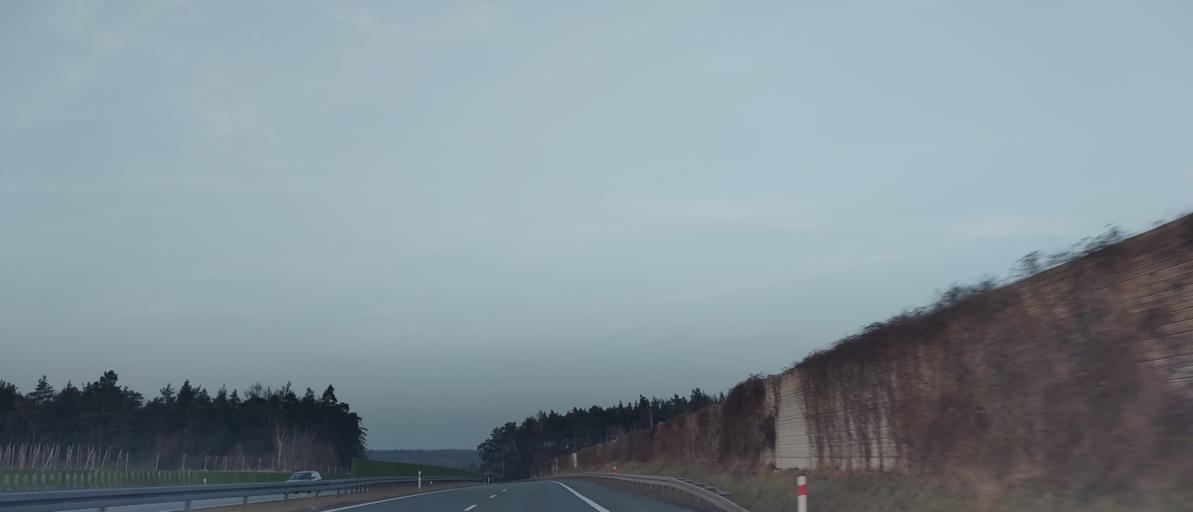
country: PL
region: Masovian Voivodeship
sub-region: Powiat grojecki
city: Grojec
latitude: 51.8931
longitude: 20.8591
